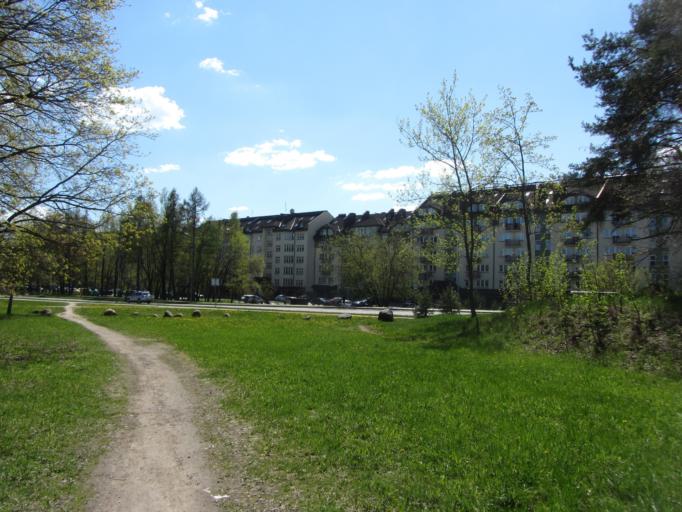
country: LT
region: Vilnius County
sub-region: Vilnius
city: Fabijoniskes
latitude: 54.7531
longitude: 25.2728
